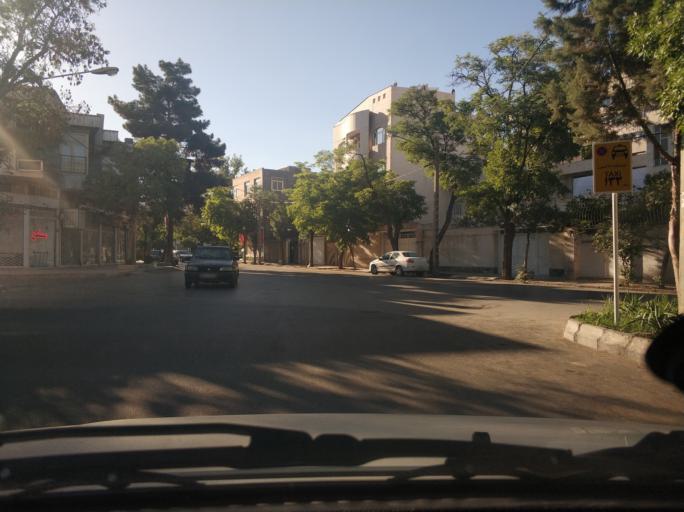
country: IR
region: Razavi Khorasan
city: Mashhad
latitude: 36.2761
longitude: 59.5938
